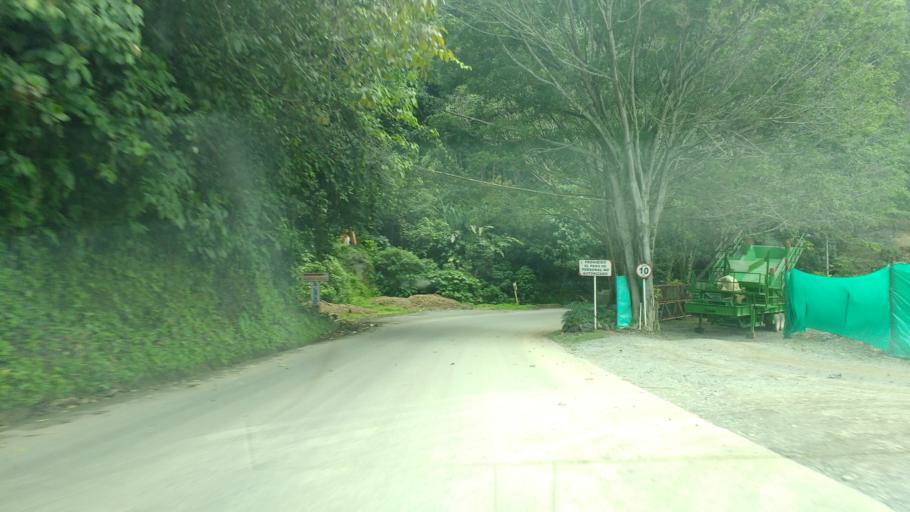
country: CO
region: Antioquia
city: Amaga
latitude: 6.0499
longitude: -75.7206
